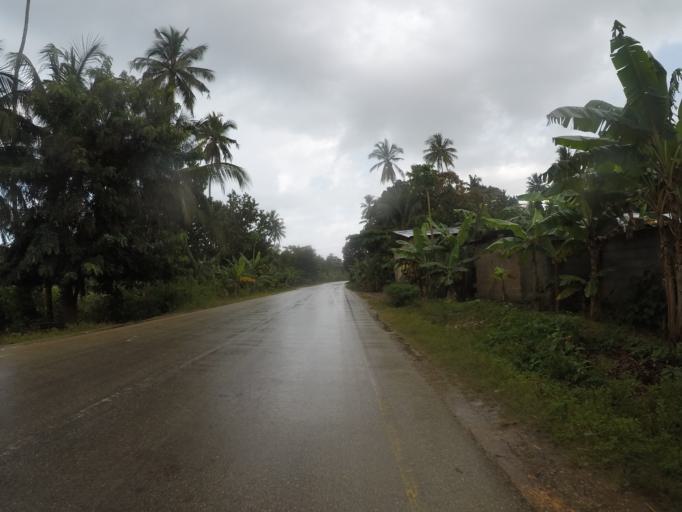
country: TZ
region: Zanzibar North
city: Mkokotoni
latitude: -5.9630
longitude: 39.1948
